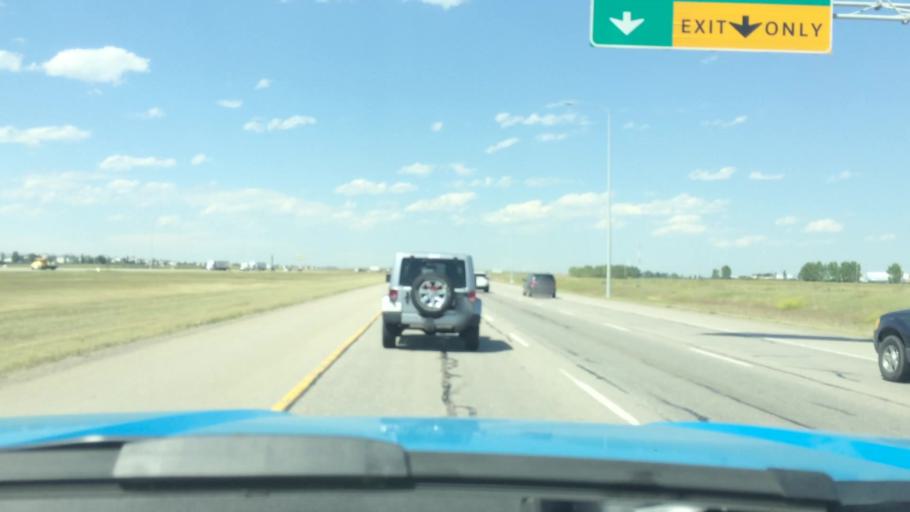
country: CA
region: Alberta
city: Chestermere
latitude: 51.0798
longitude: -113.9202
